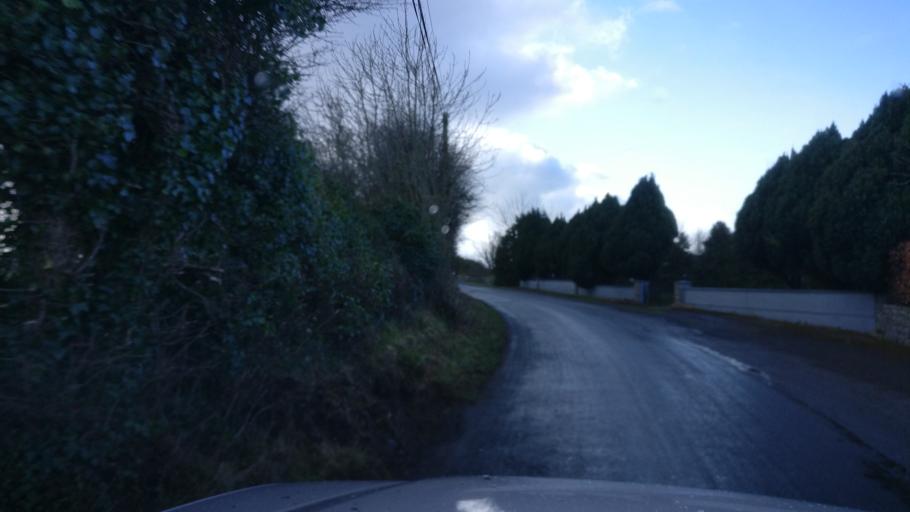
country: IE
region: Connaught
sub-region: County Galway
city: Oranmore
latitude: 53.2558
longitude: -8.9065
